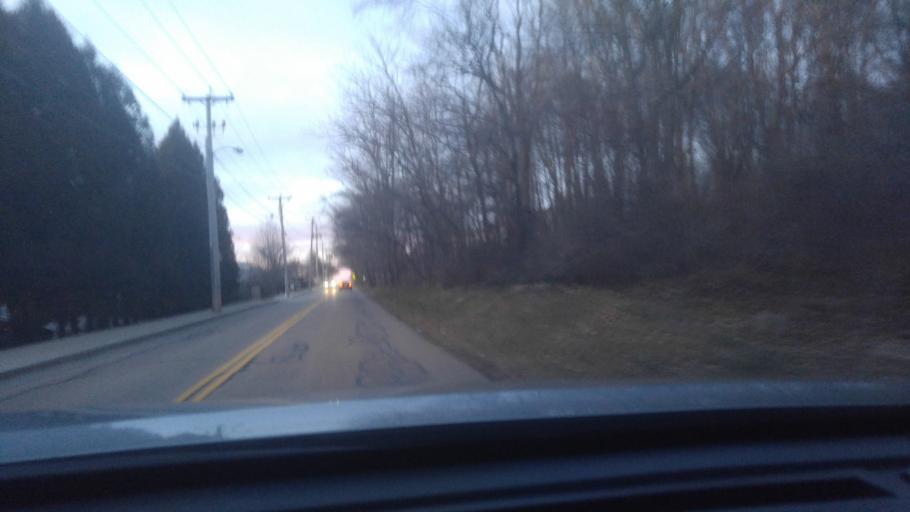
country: US
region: Rhode Island
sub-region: Newport County
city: Newport
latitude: 41.5107
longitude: -71.3128
